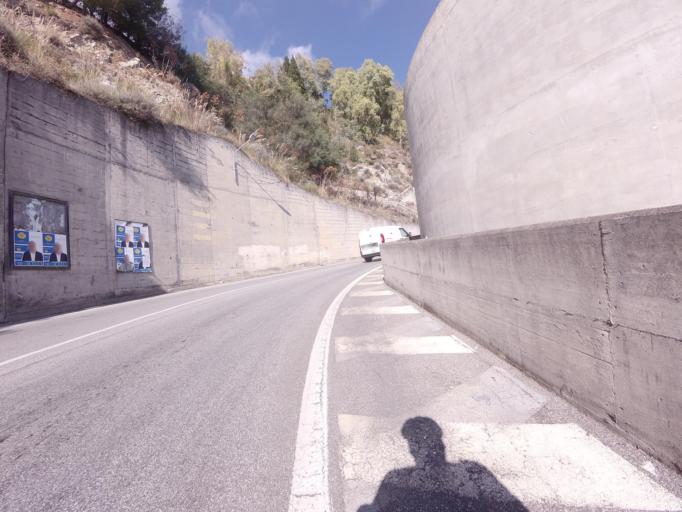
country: IT
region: Sicily
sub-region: Messina
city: Castelmola
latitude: 37.8510
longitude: 15.2792
